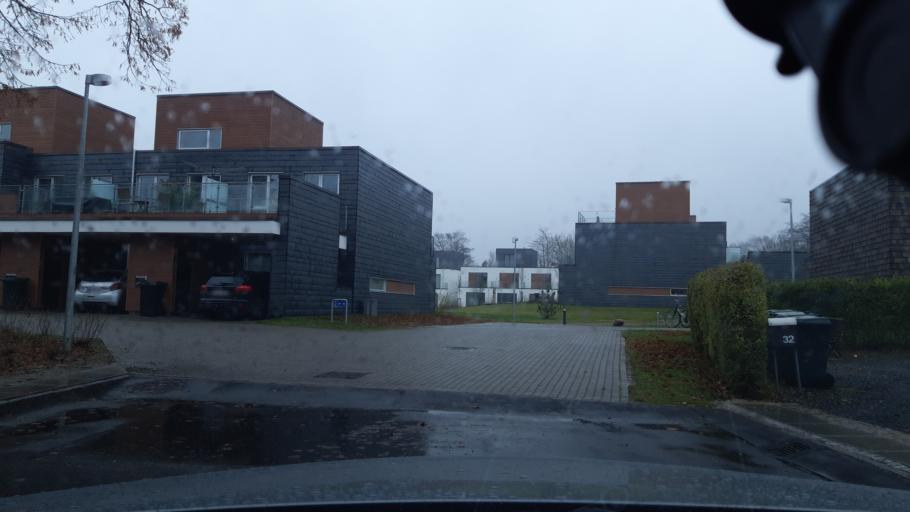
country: DK
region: Capital Region
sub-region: Herlev Kommune
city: Herlev
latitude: 55.7602
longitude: 12.4493
